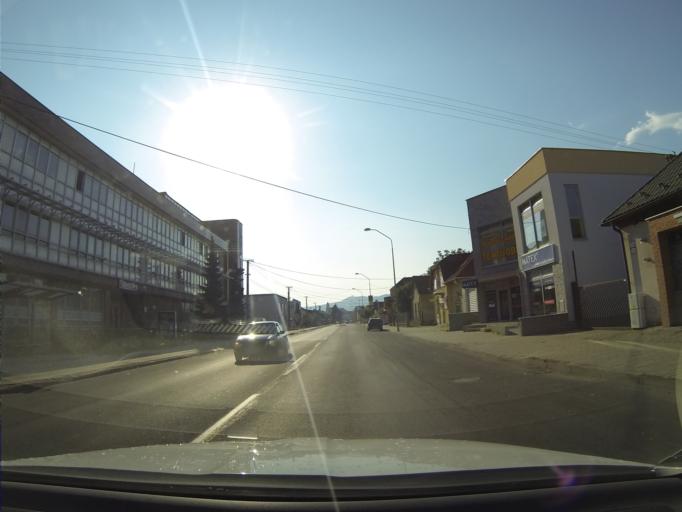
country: SK
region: Nitriansky
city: Prievidza
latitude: 48.7753
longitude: 18.6093
